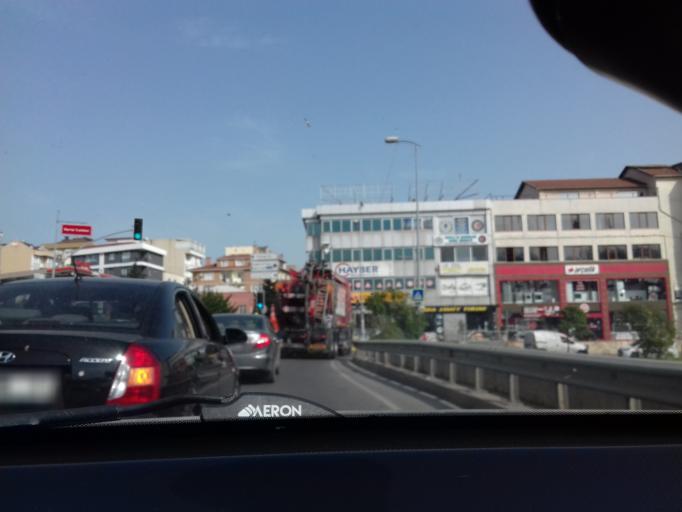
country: TR
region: Istanbul
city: Maltepe
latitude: 40.9104
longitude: 29.2152
